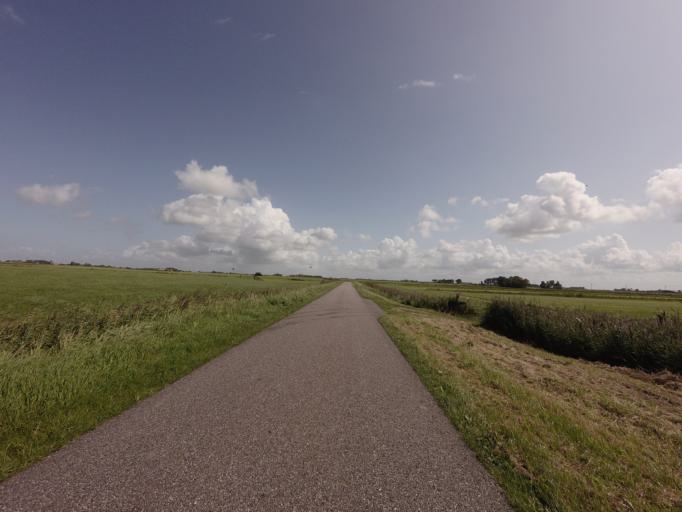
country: NL
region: Friesland
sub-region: Sudwest Fryslan
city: Makkum
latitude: 53.0651
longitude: 5.4401
